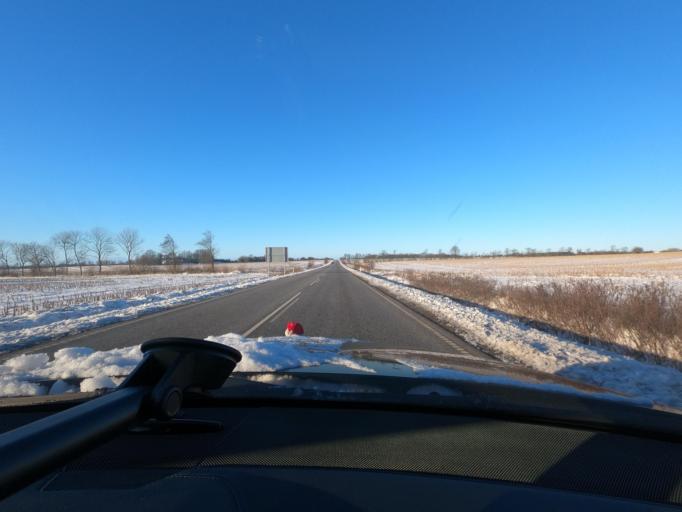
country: DK
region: South Denmark
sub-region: Tonder Kommune
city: Toftlund
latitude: 55.1105
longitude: 9.1751
